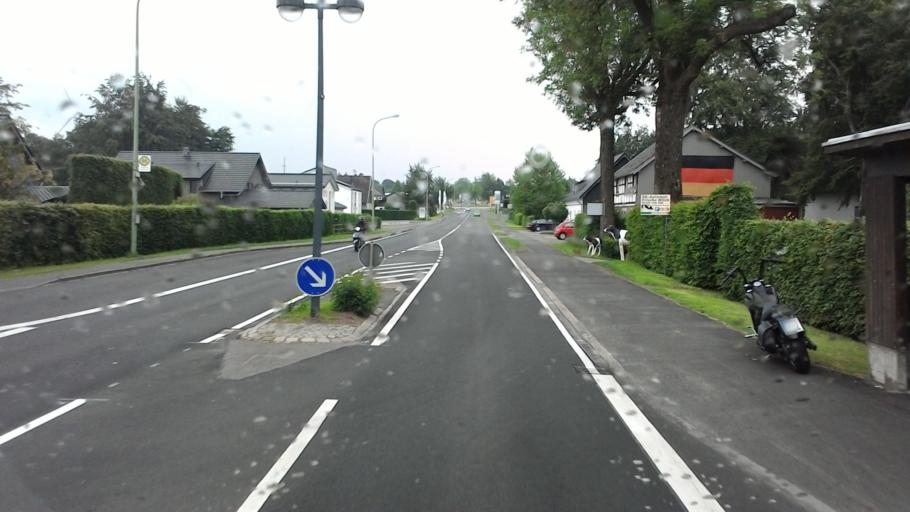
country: DE
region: North Rhine-Westphalia
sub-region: Regierungsbezirk Koln
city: Monschau
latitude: 50.5821
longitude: 6.2582
